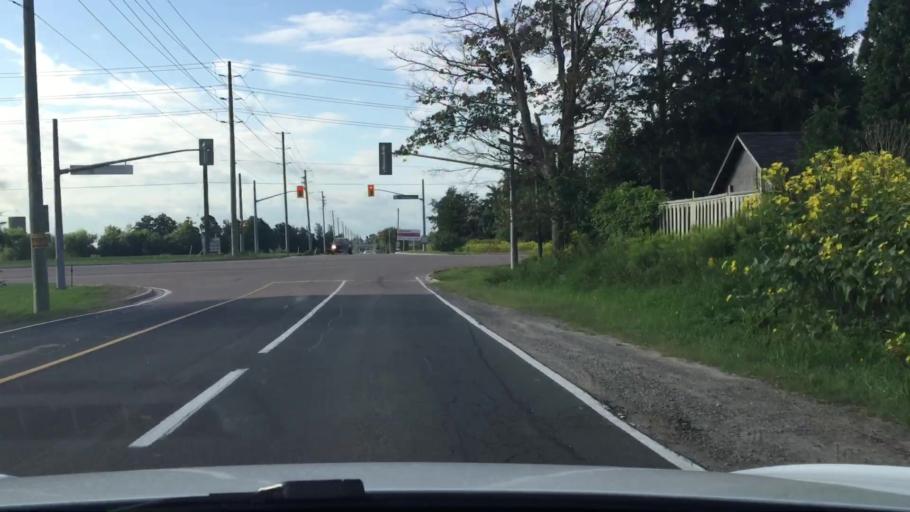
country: CA
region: Ontario
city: Markham
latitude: 43.8840
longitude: -79.2105
